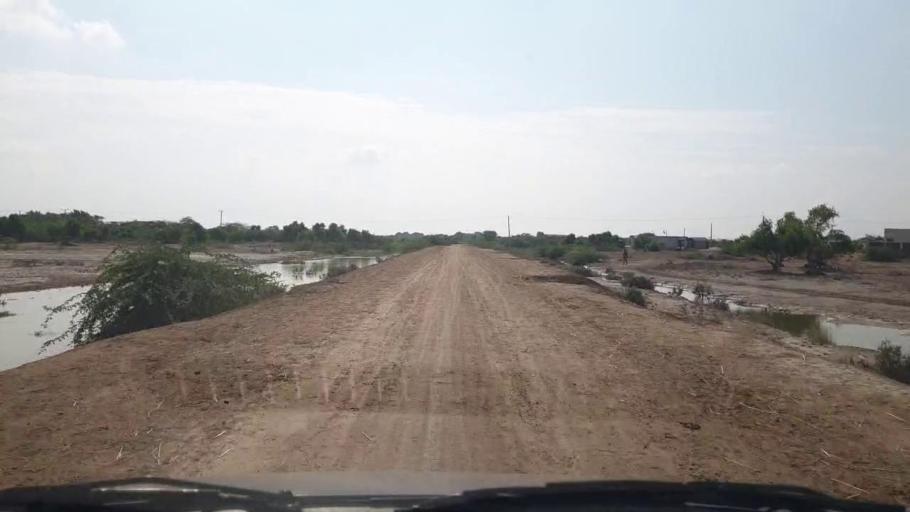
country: PK
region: Sindh
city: Badin
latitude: 24.4809
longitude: 68.6127
